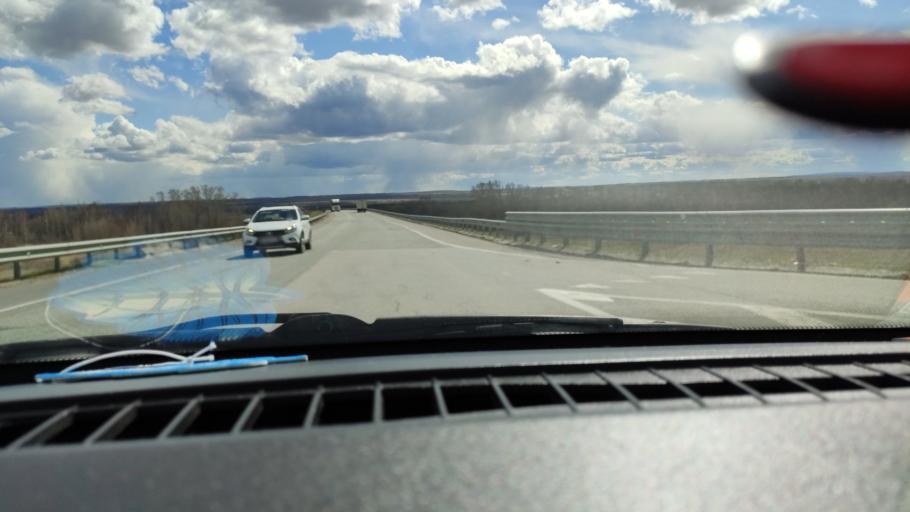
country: RU
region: Samara
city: Varlamovo
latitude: 53.1650
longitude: 48.2818
